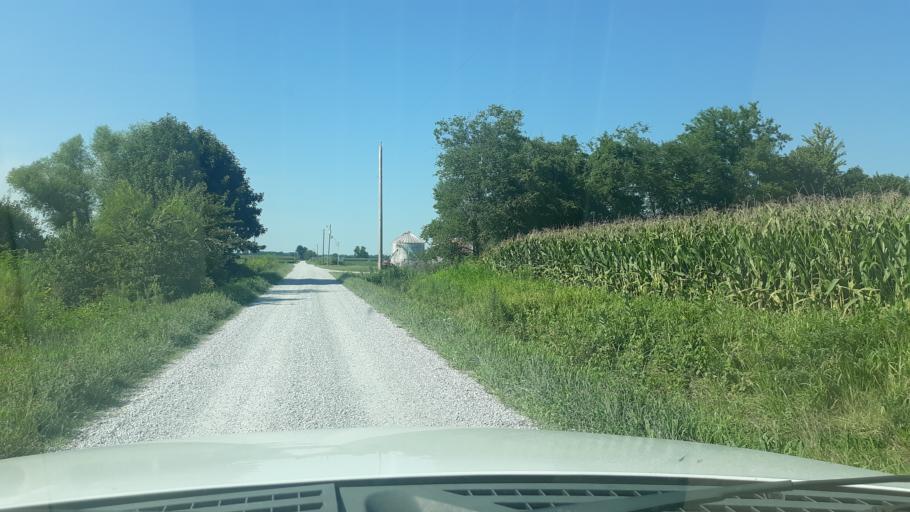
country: US
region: Illinois
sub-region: Saline County
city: Eldorado
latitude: 37.8504
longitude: -88.4849
